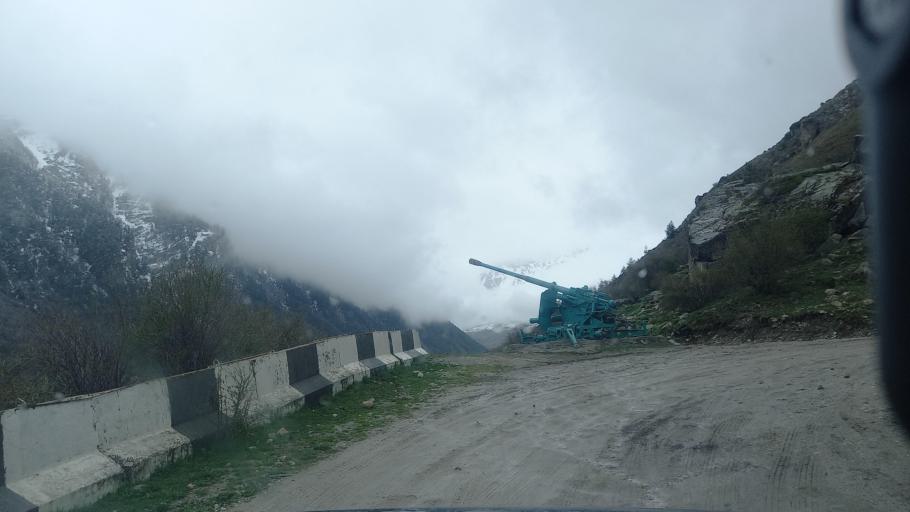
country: RU
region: Kabardino-Balkariya
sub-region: El'brusskiy Rayon
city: El'brus
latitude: 43.2266
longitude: 42.6635
